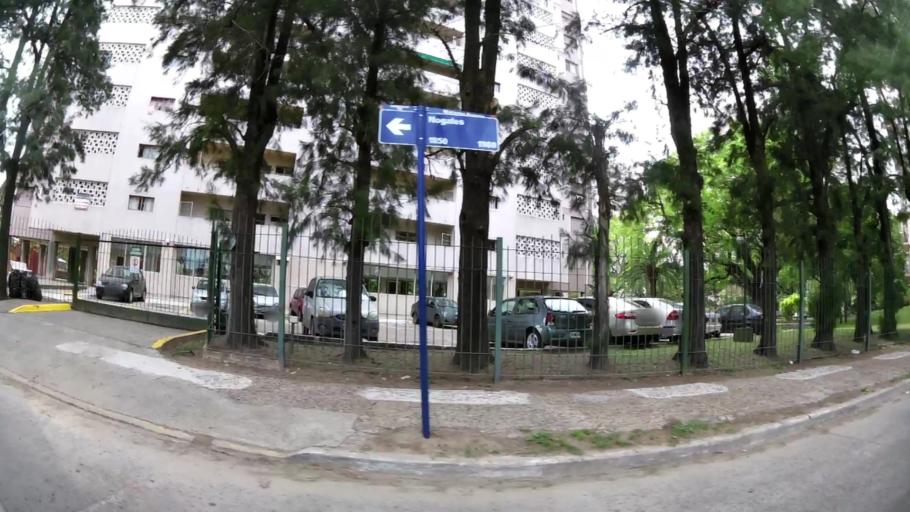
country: AR
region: Buenos Aires F.D.
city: Villa Lugano
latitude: -34.7076
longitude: -58.5049
